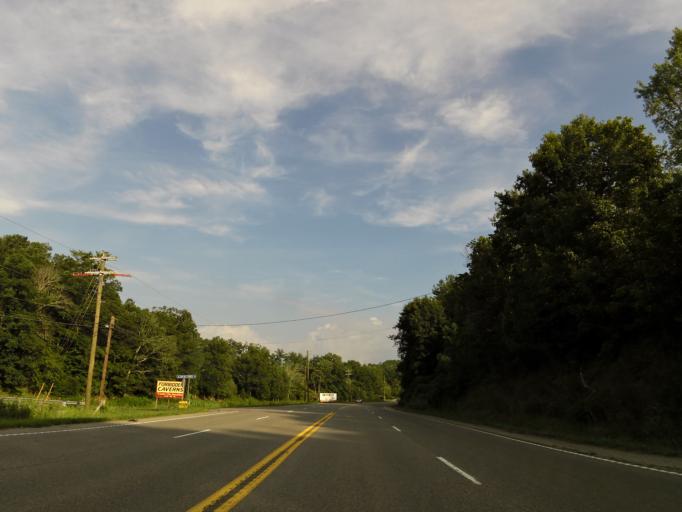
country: US
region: Tennessee
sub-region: Sevier County
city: Seymour
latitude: 35.8635
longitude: -83.6559
